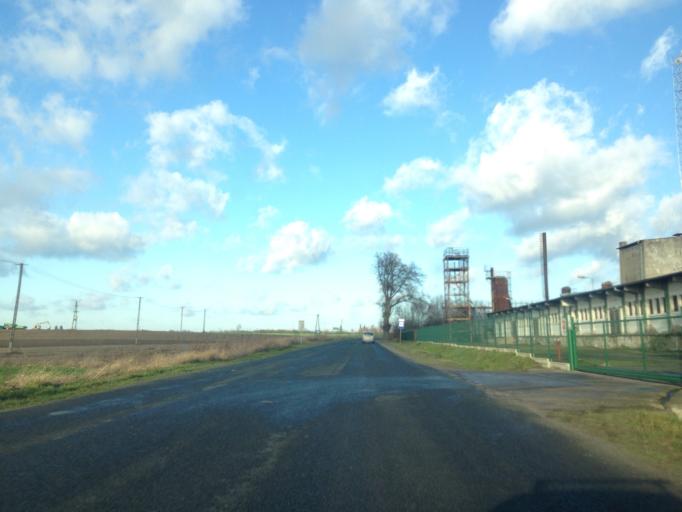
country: PL
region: Kujawsko-Pomorskie
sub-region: Powiat grudziadzki
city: Lasin
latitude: 53.5298
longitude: 19.0721
